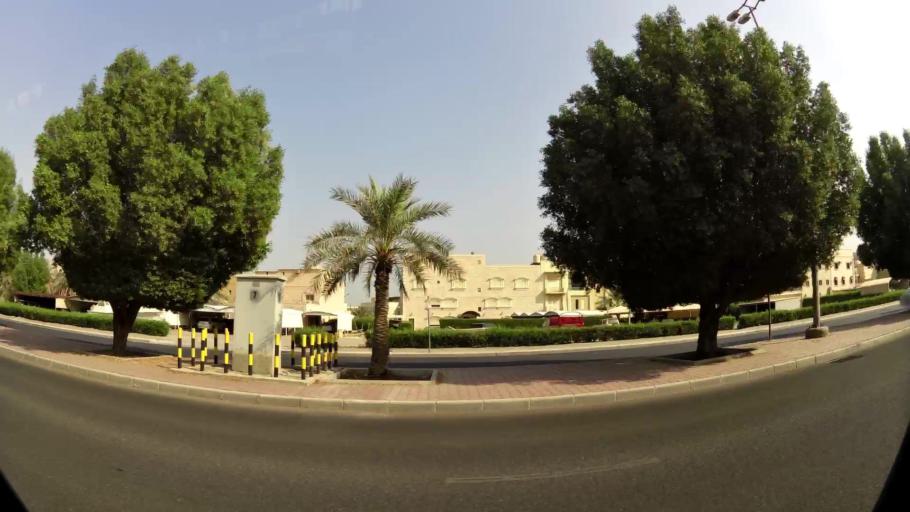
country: KW
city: Bayan
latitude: 29.2957
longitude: 48.0498
